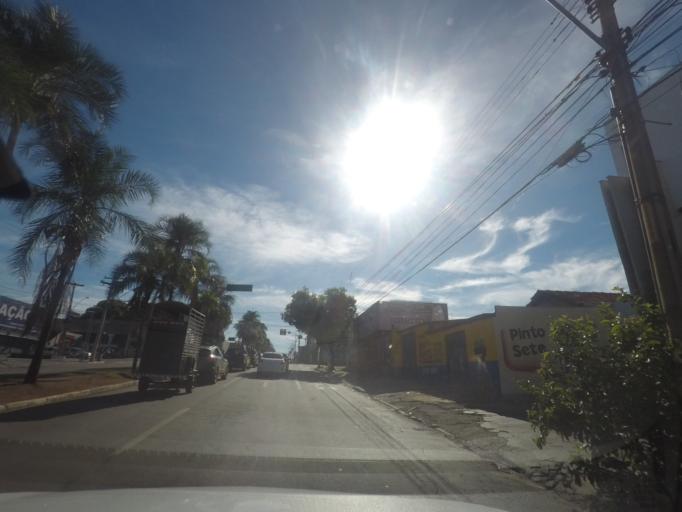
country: BR
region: Goias
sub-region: Goiania
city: Goiania
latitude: -16.6659
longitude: -49.2670
